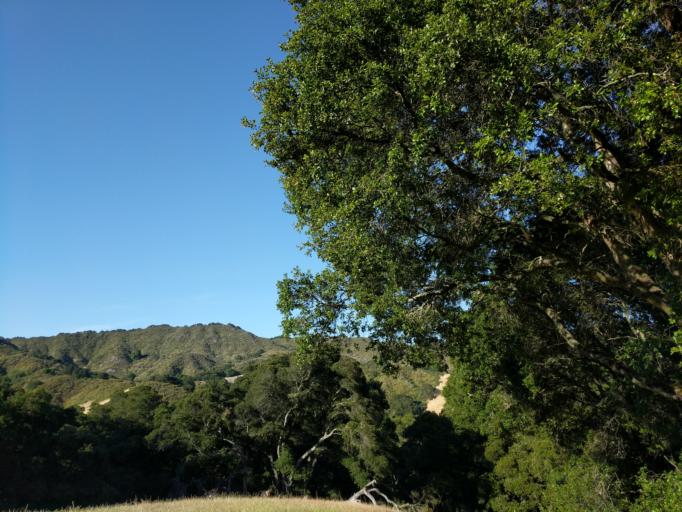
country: US
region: California
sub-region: Contra Costa County
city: Alamo
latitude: 37.8119
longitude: -122.0480
